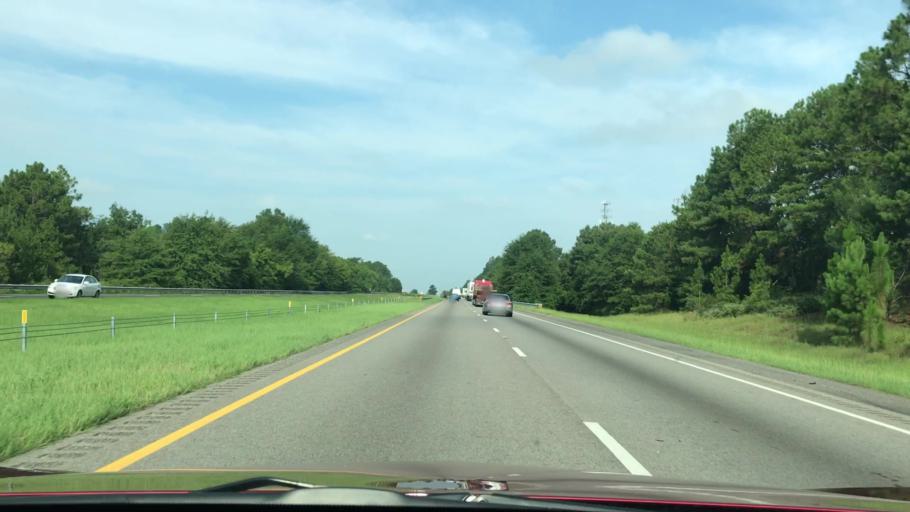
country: US
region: South Carolina
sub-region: Aiken County
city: Graniteville
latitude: 33.6341
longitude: -81.7797
